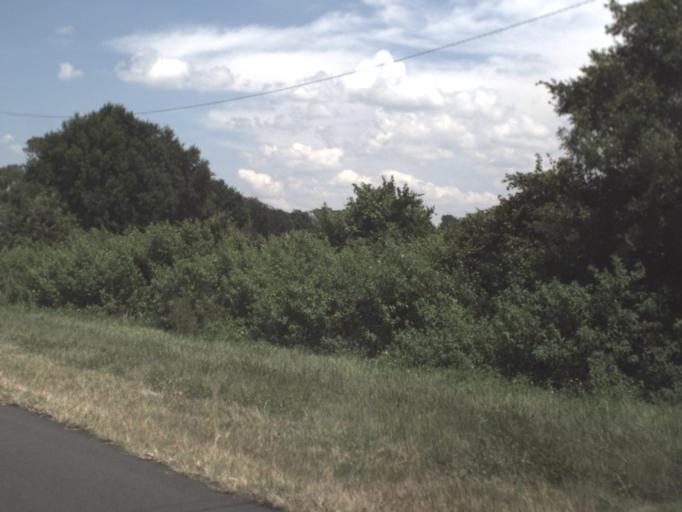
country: US
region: Florida
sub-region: Hillsborough County
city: Ruskin
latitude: 27.6504
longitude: -82.5144
